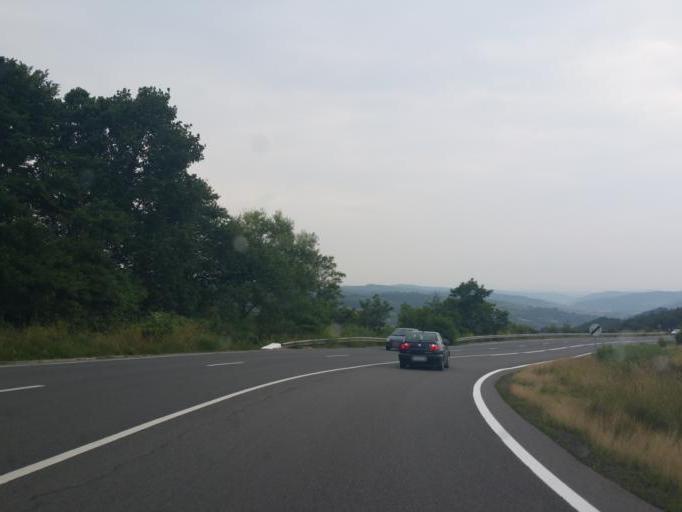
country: RO
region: Cluj
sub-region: Comuna Sanpaul
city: Sanpaul
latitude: 46.9449
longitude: 23.3808
